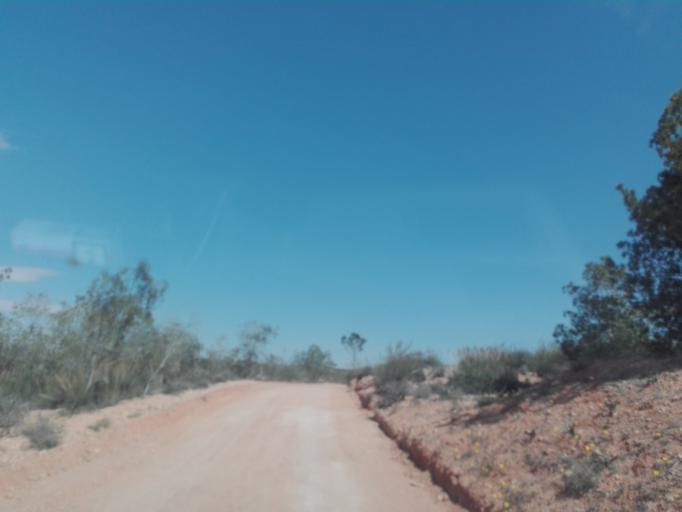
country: TN
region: Safaqis
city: Sfax
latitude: 34.6966
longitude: 10.5303
